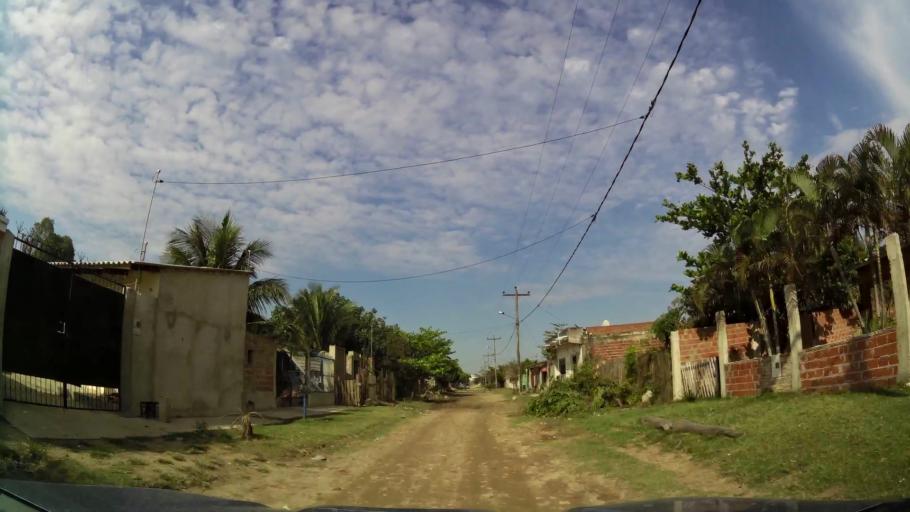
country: BO
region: Santa Cruz
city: Santa Cruz de la Sierra
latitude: -17.7349
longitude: -63.1335
